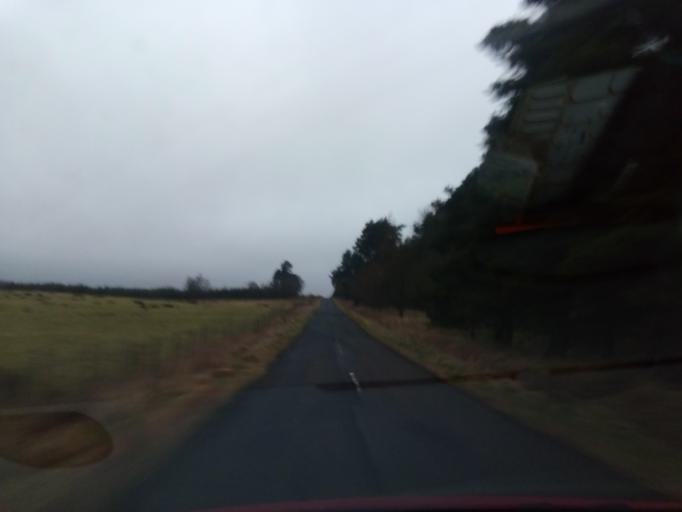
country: GB
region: England
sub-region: Northumberland
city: Rothley
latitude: 55.2032
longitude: -2.0038
